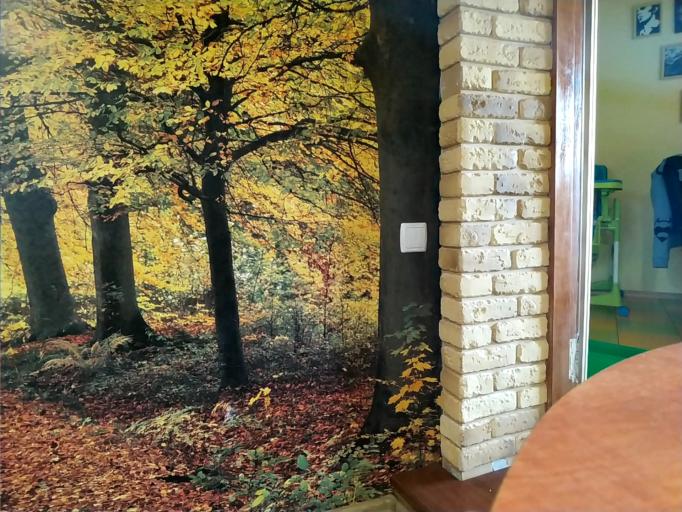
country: RU
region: Leningrad
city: Luga
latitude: 58.9682
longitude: 29.5558
